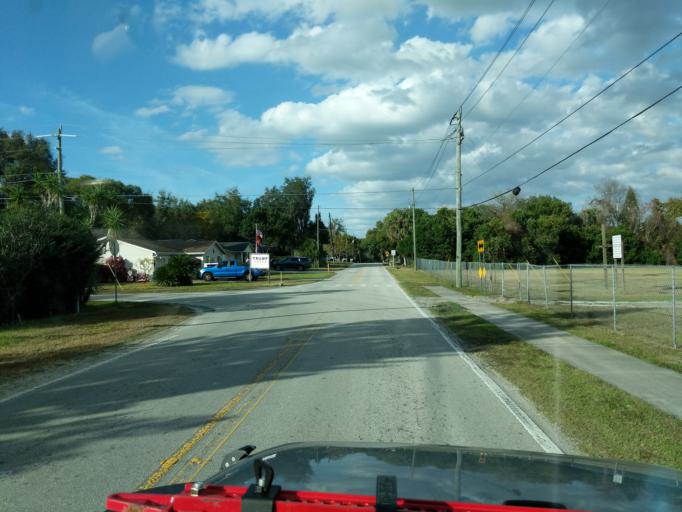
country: US
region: Florida
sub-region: Seminole County
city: Geneva
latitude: 28.7414
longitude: -81.1153
